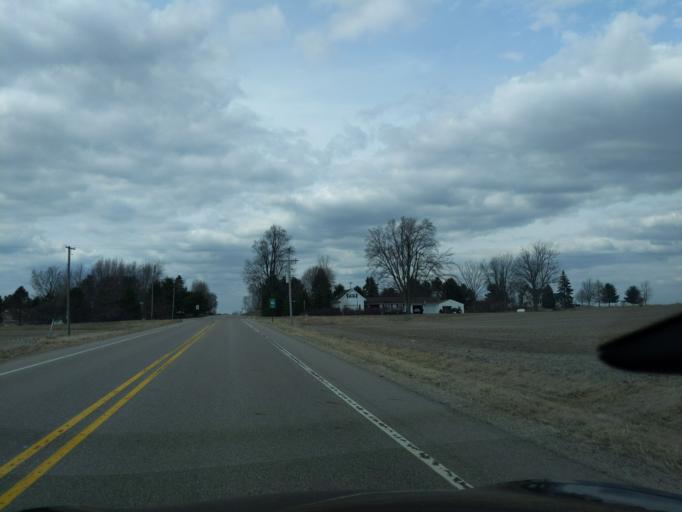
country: US
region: Michigan
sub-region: Ingham County
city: Mason
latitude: 42.5594
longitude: -84.4832
